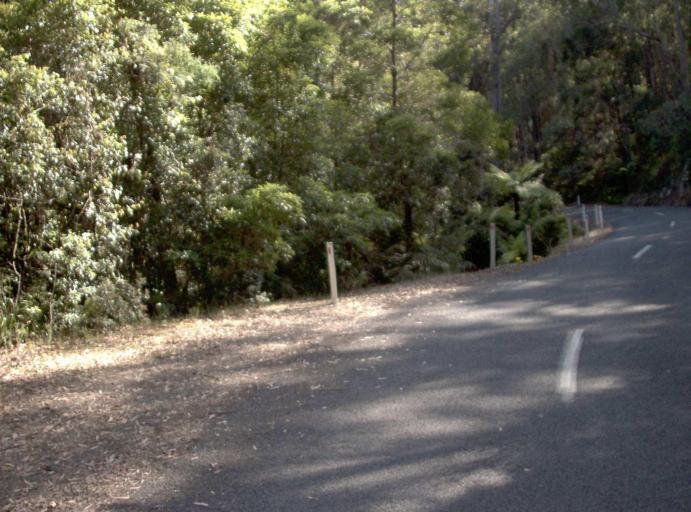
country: AU
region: Victoria
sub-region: East Gippsland
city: Lakes Entrance
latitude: -37.4547
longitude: 148.5760
